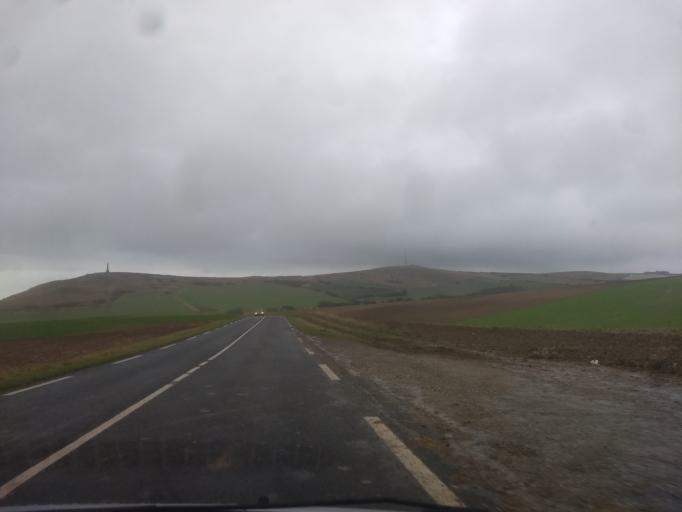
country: FR
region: Nord-Pas-de-Calais
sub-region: Departement du Pas-de-Calais
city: Wissant
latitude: 50.9126
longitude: 1.7018
